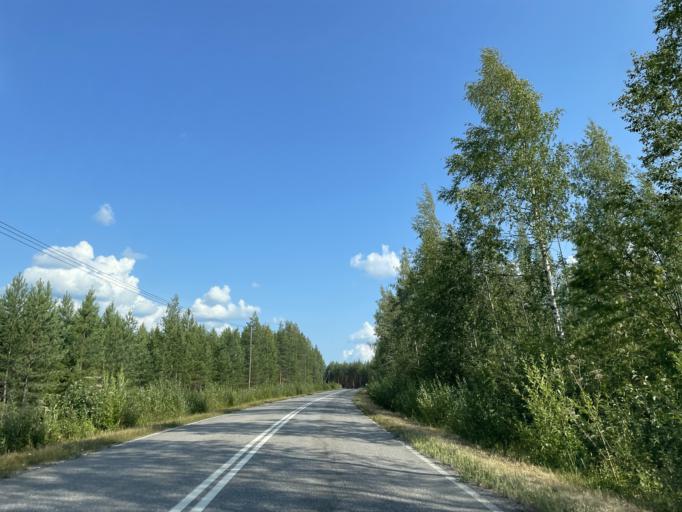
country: FI
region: Central Finland
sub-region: Saarijaervi-Viitasaari
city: Pihtipudas
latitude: 63.3520
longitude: 25.7850
